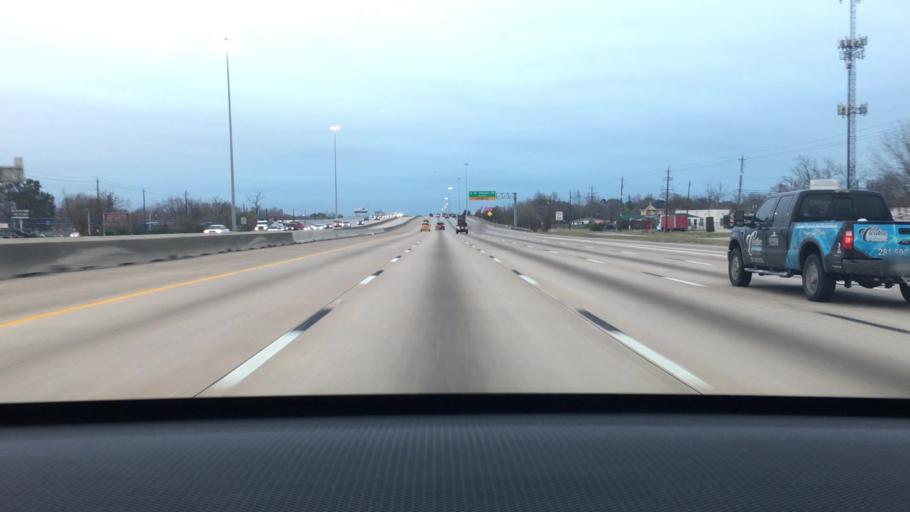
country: US
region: Texas
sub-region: Harris County
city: Aldine
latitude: 29.8749
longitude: -95.3272
